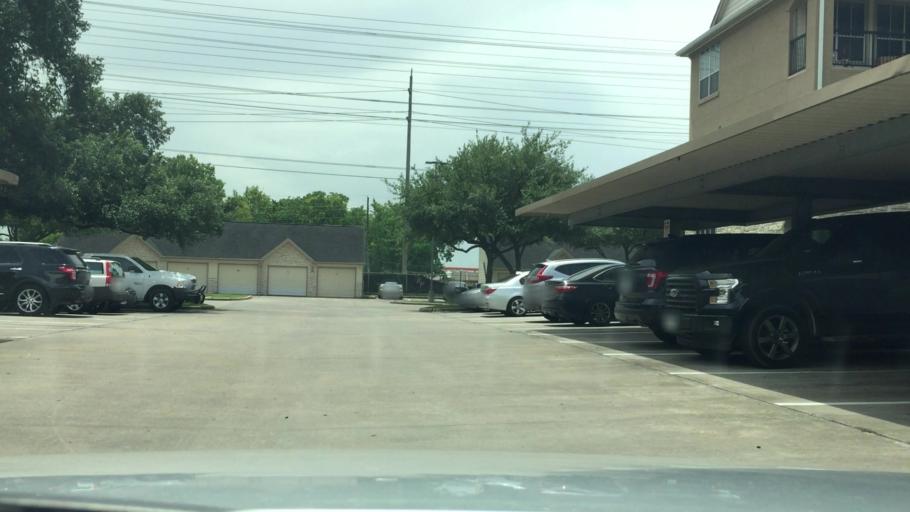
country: US
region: Texas
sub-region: Harris County
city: Bellaire
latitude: 29.7227
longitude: -95.4700
